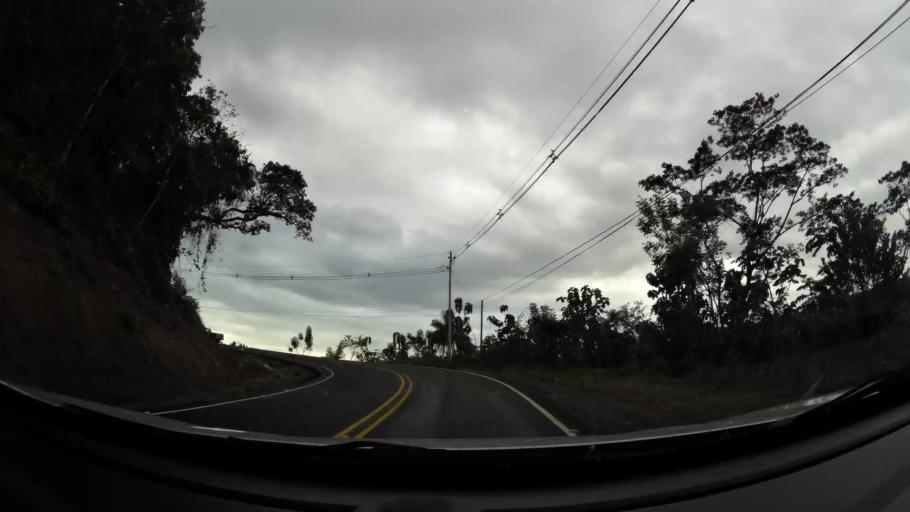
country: CR
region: Alajuela
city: Orotina
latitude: 9.9491
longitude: -84.5714
